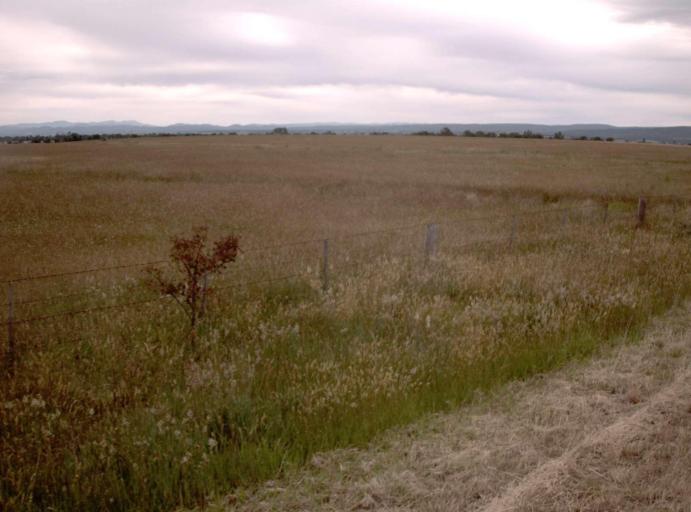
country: AU
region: Victoria
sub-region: East Gippsland
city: Bairnsdale
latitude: -37.8772
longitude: 147.5597
